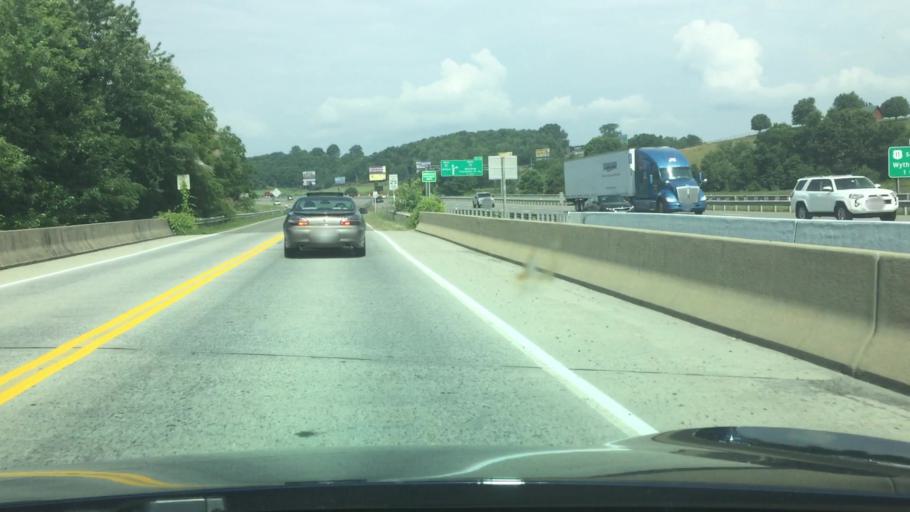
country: US
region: Virginia
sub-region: Wythe County
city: Wytheville
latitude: 36.9458
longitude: -81.0322
